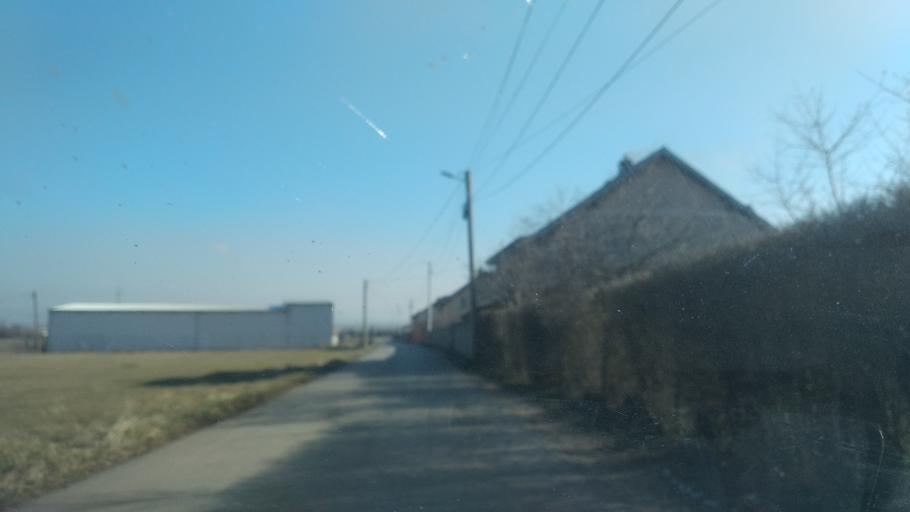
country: XK
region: Pristina
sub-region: Komuna e Gracanices
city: Glanica
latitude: 42.5828
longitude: 21.0125
